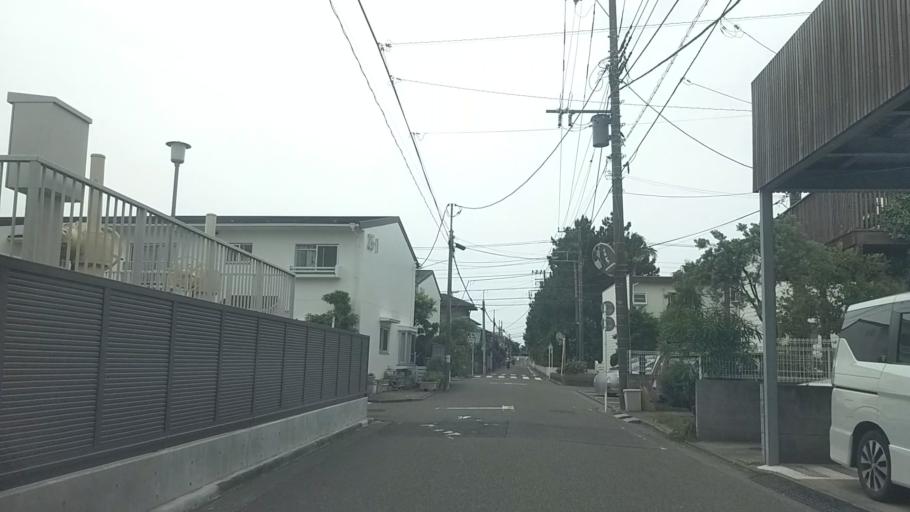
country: JP
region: Kanagawa
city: Fujisawa
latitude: 35.3203
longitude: 139.4602
